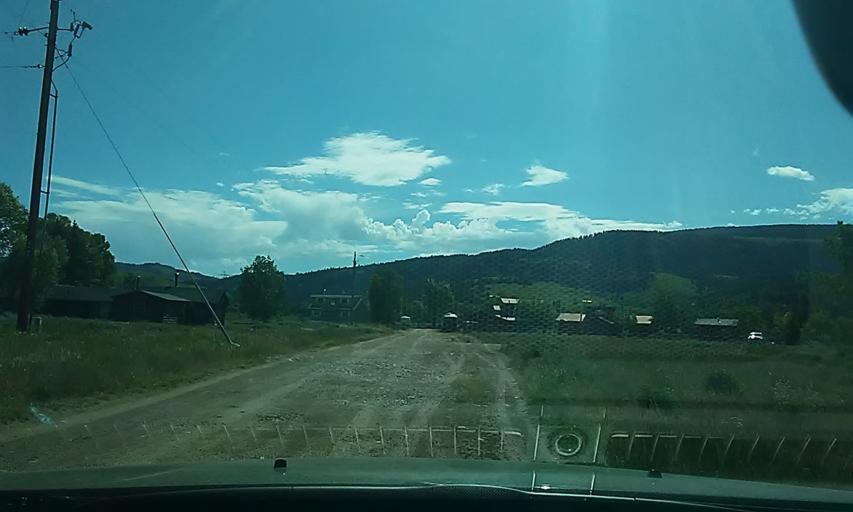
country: US
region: Wyoming
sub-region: Teton County
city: Jackson
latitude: 43.6228
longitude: -110.6230
